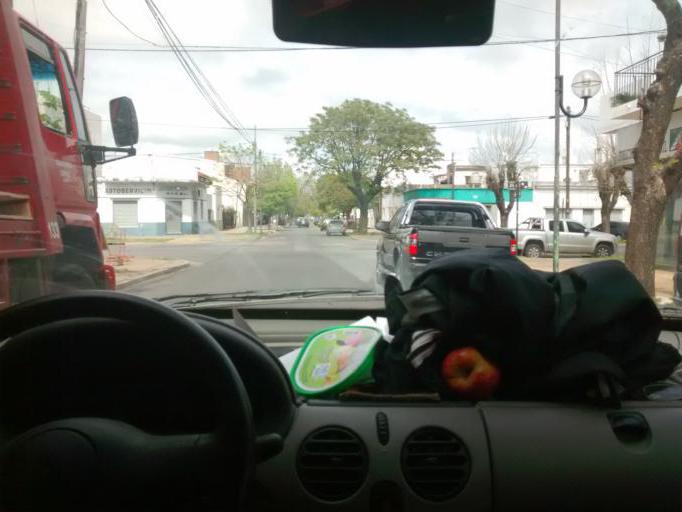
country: AR
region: Buenos Aires
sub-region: Partido de La Plata
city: La Plata
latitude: -34.9443
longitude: -57.9507
